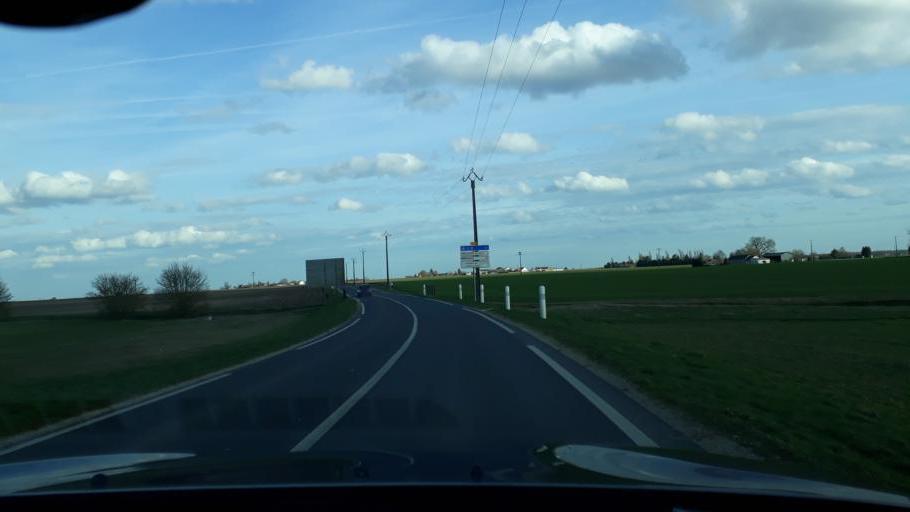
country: FR
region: Centre
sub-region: Departement du Loiret
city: Neuville-aux-Bois
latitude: 48.0699
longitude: 2.0704
